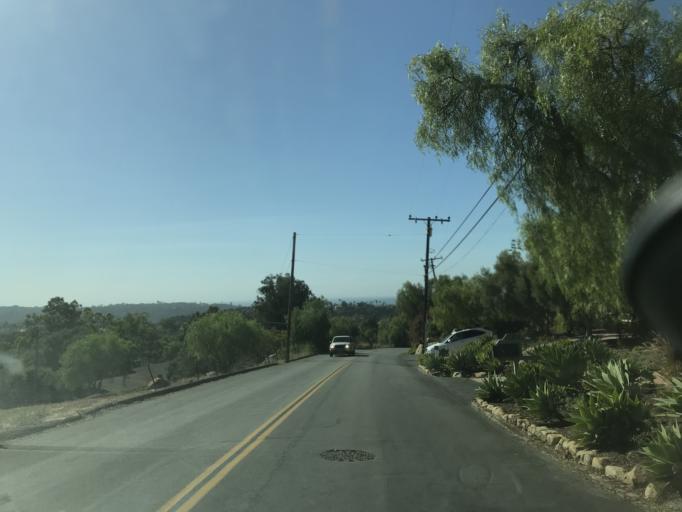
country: US
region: California
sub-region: Santa Barbara County
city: Goleta
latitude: 34.4627
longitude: -119.7788
